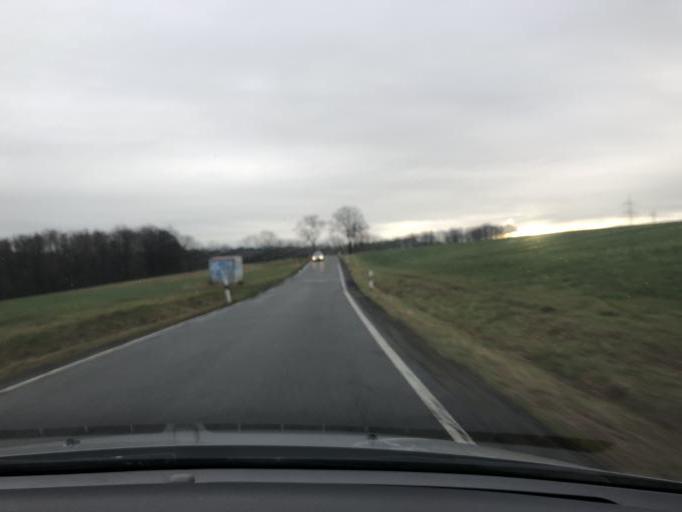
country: DE
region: Saxony
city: Niederfrohna
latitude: 50.8825
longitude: 12.7139
